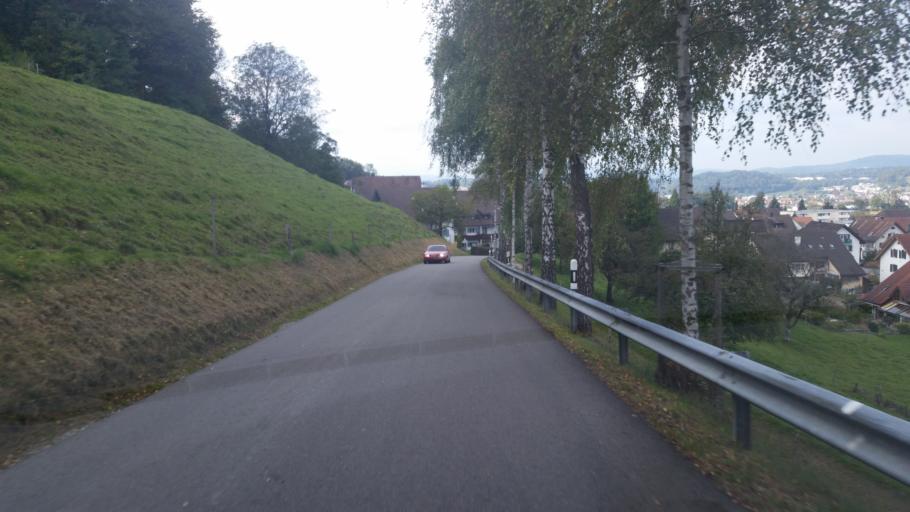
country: CH
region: Aargau
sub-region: Bezirk Baden
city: Mellingen
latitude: 47.4002
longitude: 8.2786
